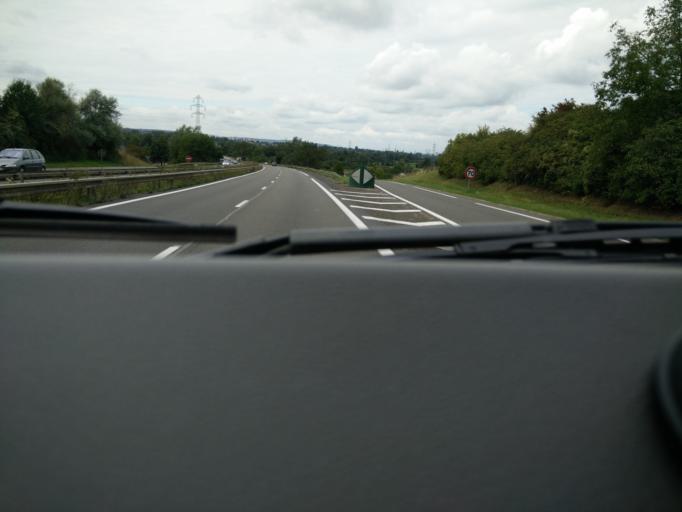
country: FR
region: Champagne-Ardenne
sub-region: Departement des Ardennes
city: Lumes
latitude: 49.7381
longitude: 4.7872
